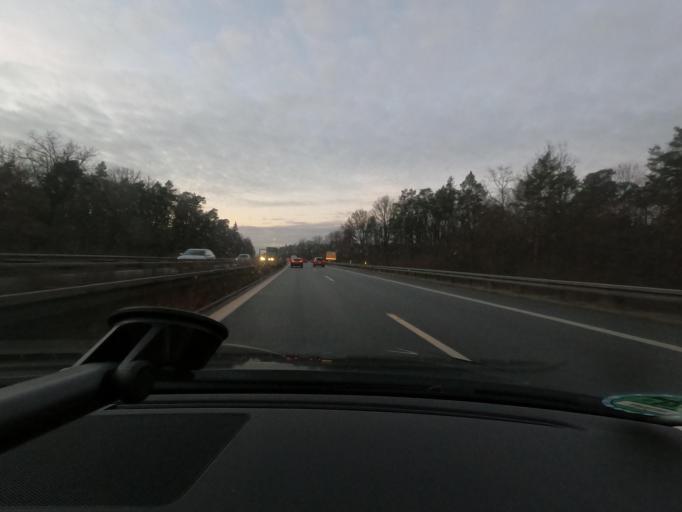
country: DE
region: Bavaria
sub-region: Upper Franconia
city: Gundelsheim
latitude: 49.9464
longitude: 10.9021
